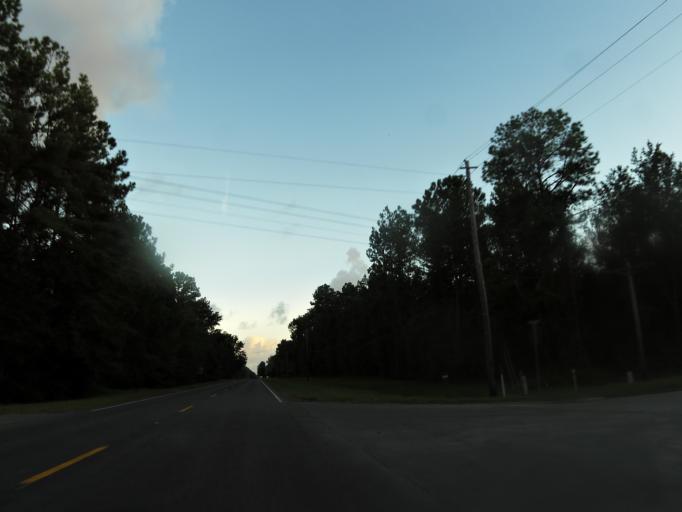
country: US
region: Georgia
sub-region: Camden County
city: Woodbine
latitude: 30.9194
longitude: -81.7138
